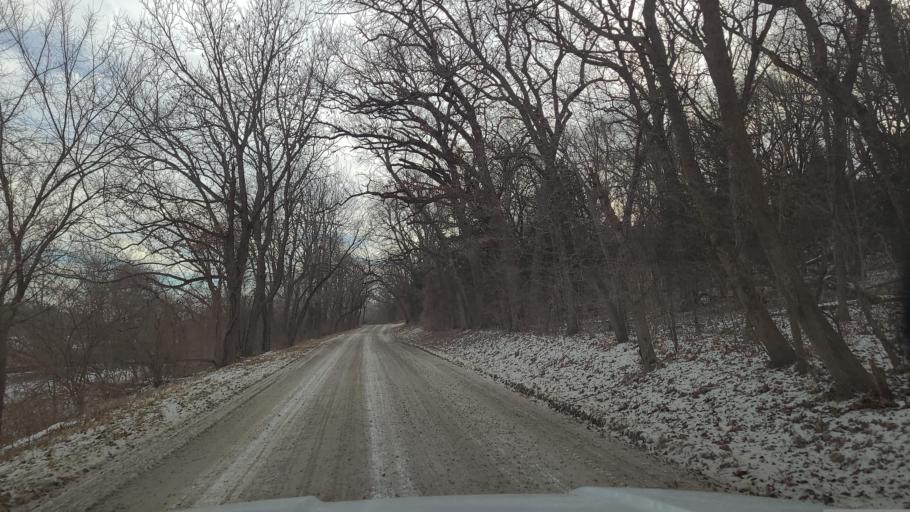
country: US
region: Kansas
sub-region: Douglas County
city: Lawrence
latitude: 39.0320
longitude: -95.3491
